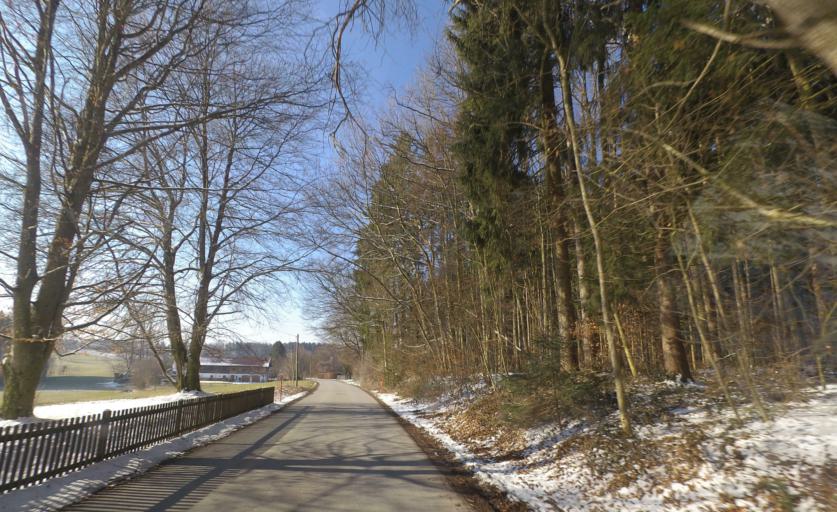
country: DE
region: Bavaria
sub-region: Upper Bavaria
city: Seeon-Seebruck
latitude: 47.9306
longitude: 12.5015
